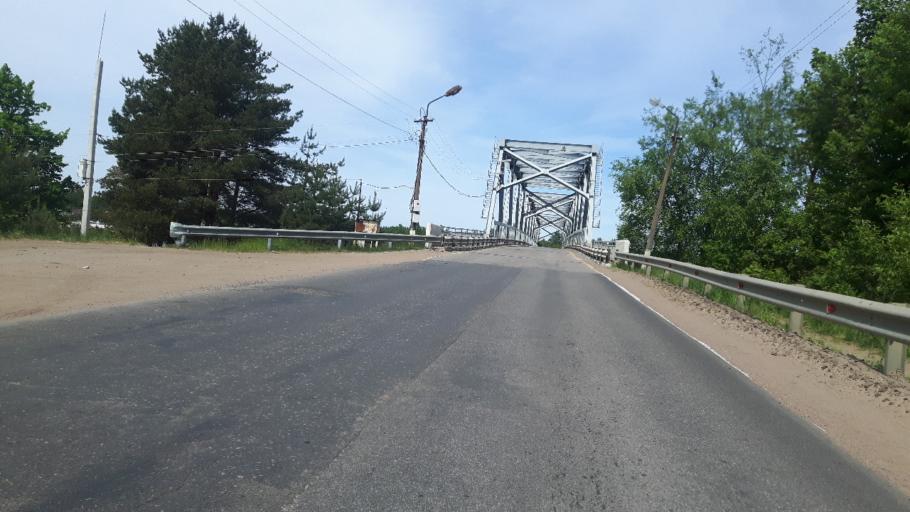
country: RU
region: Leningrad
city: Ust'-Luga
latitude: 59.6518
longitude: 28.2593
